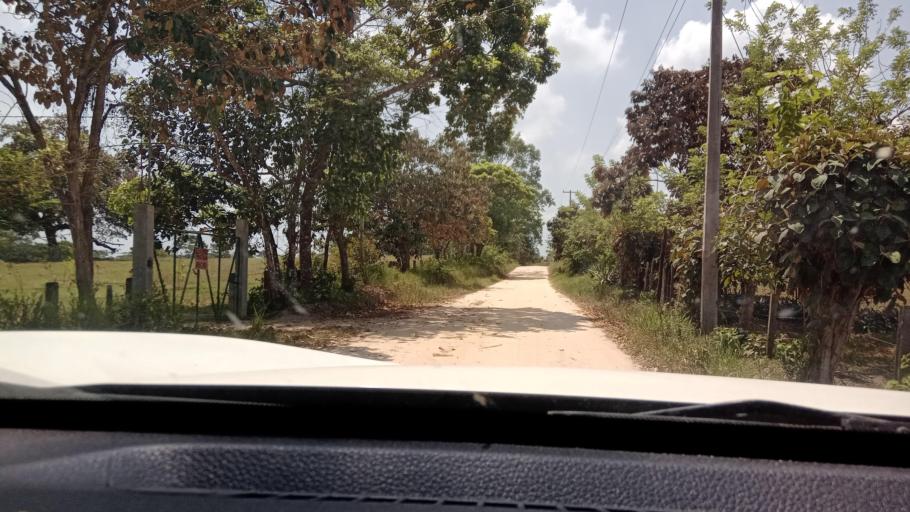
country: MX
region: Veracruz
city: Las Choapas
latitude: 17.9429
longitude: -94.1237
